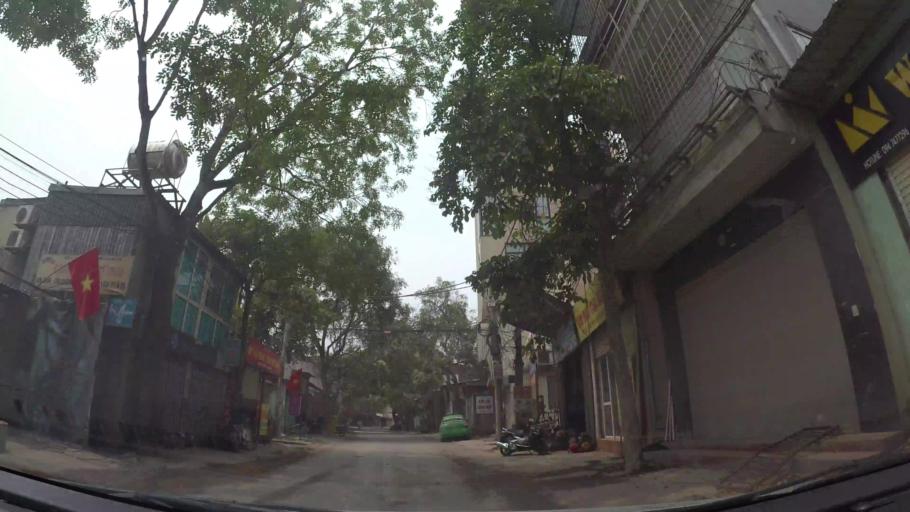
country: VN
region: Ha Noi
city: Cau Dien
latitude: 21.0288
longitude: 105.7406
